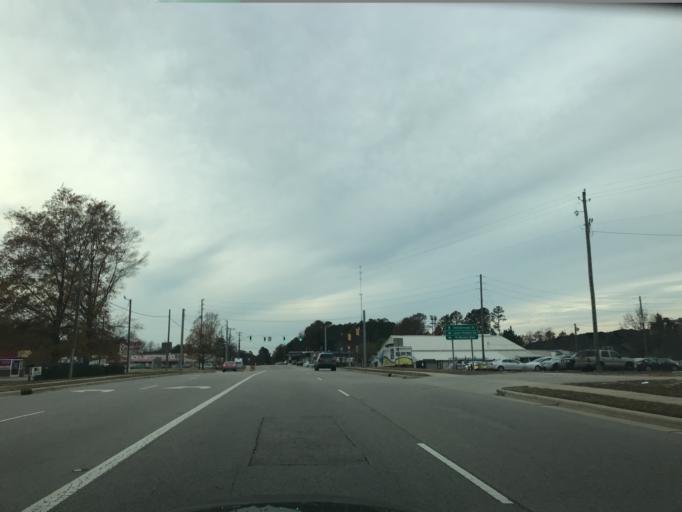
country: US
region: North Carolina
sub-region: Wake County
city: West Raleigh
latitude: 35.7864
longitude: -78.7194
